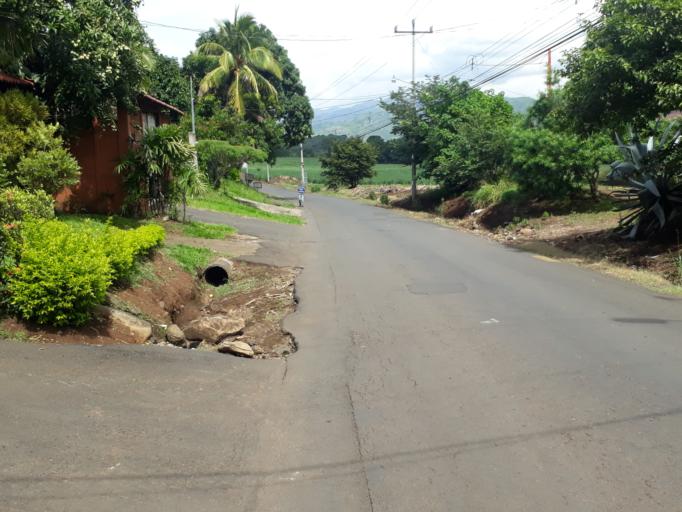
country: CR
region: Alajuela
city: Carrillos
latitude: 10.0247
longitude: -84.3326
